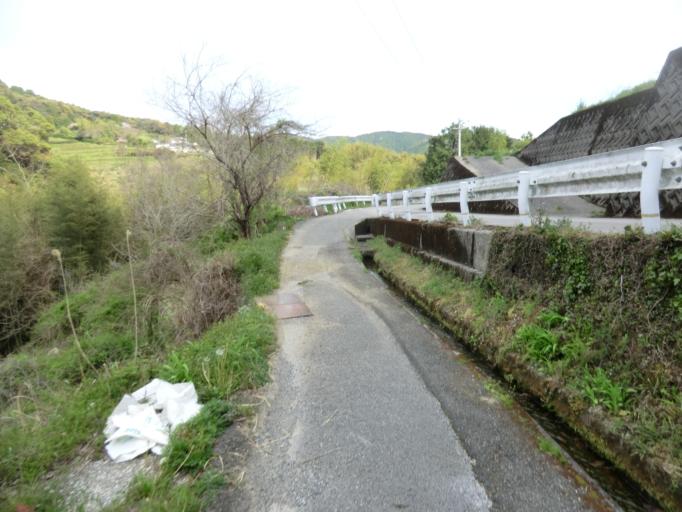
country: JP
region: Kochi
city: Kochi-shi
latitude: 33.6423
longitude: 133.7191
